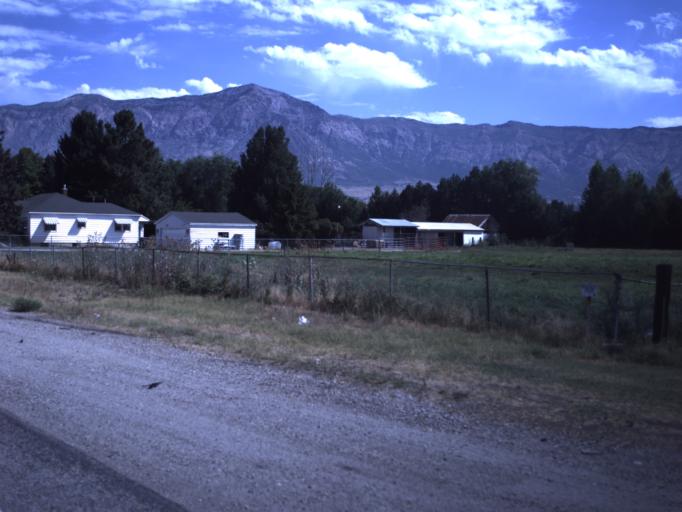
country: US
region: Utah
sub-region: Weber County
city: Farr West
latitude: 41.2837
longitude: -112.0280
